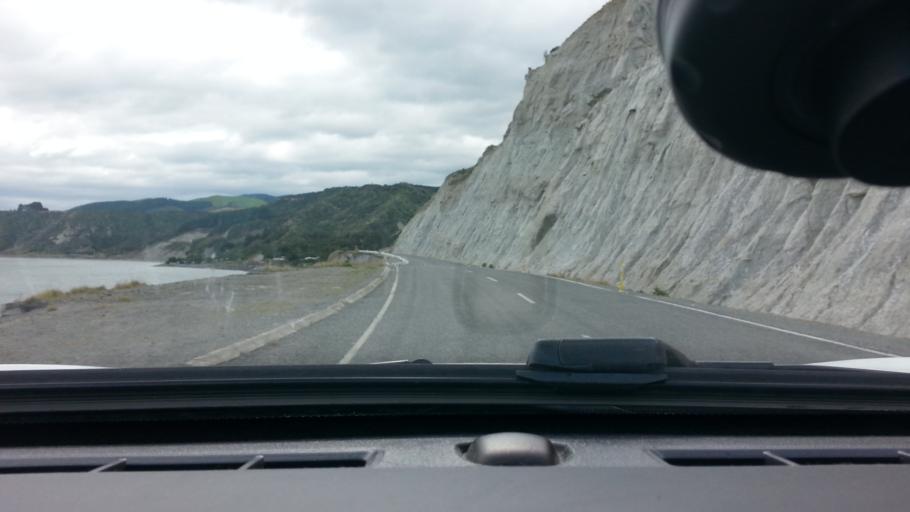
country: NZ
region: Wellington
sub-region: South Wairarapa District
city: Waipawa
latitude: -41.4661
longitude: 175.2150
